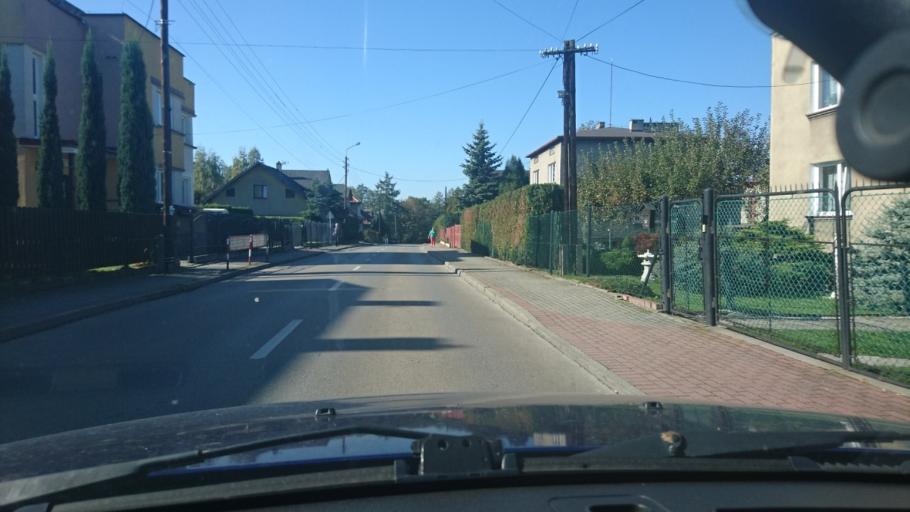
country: PL
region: Silesian Voivodeship
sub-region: Powiat bielski
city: Czechowice-Dziedzice
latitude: 49.9093
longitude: 18.9998
